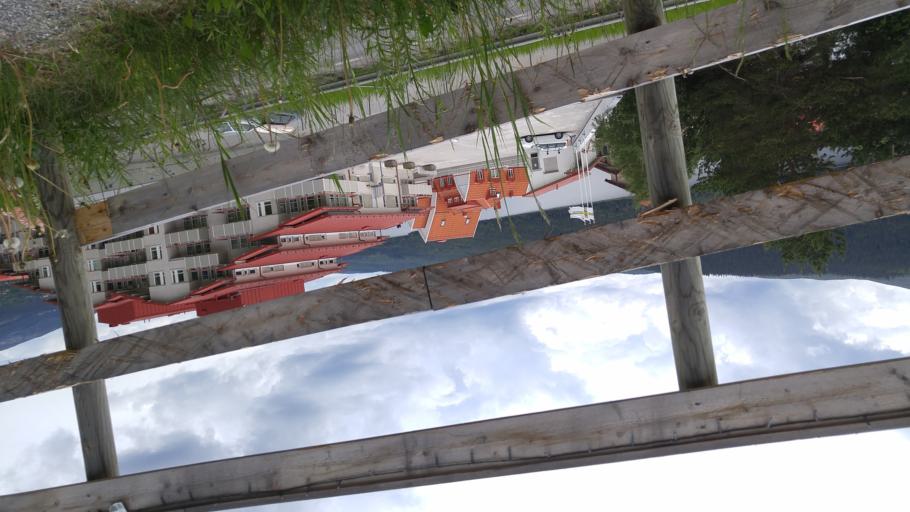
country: SE
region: Jaemtland
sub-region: Are Kommun
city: Are
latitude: 63.4013
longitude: 13.0790
